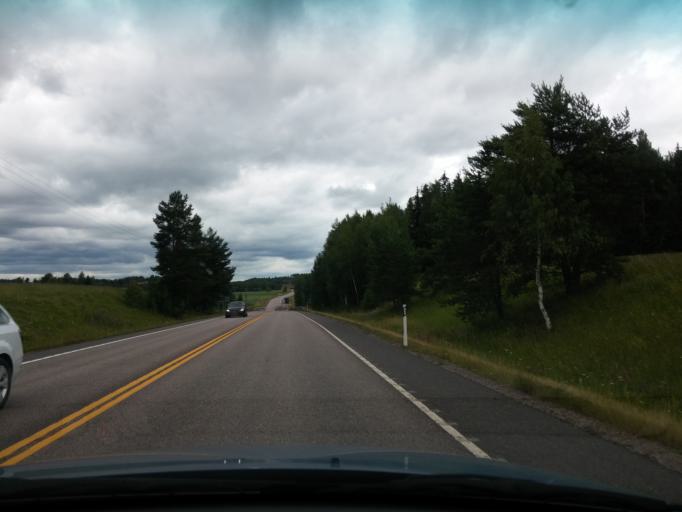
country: FI
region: Uusimaa
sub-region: Porvoo
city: Askola
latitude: 60.4505
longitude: 25.5847
